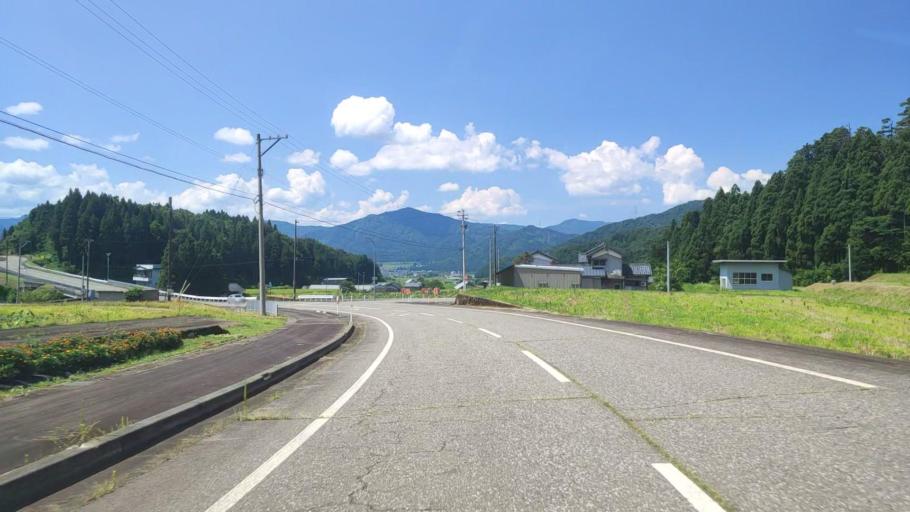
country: JP
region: Fukui
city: Katsuyama
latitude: 36.1026
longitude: 136.4923
